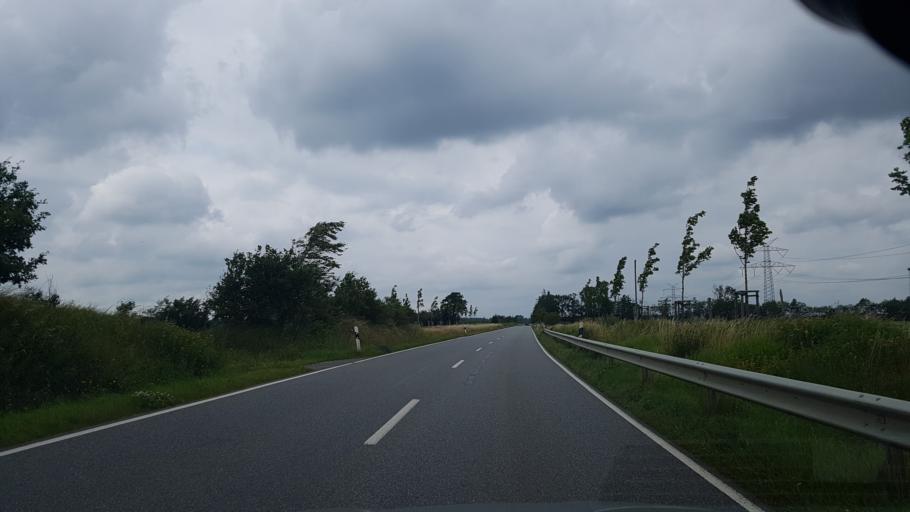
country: DE
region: Schleswig-Holstein
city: Osterby
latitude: 54.8054
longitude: 9.2396
